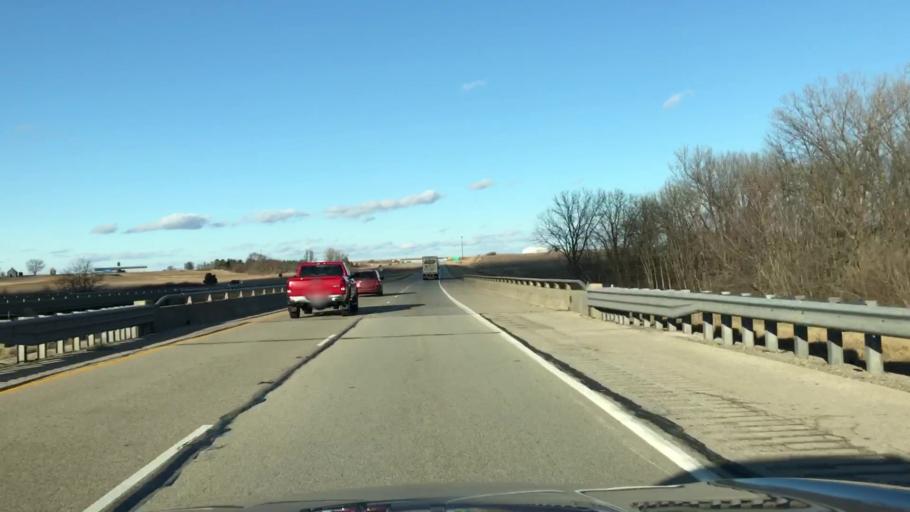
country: US
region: Illinois
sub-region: McLean County
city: Lexington
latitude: 40.6350
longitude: -88.8142
